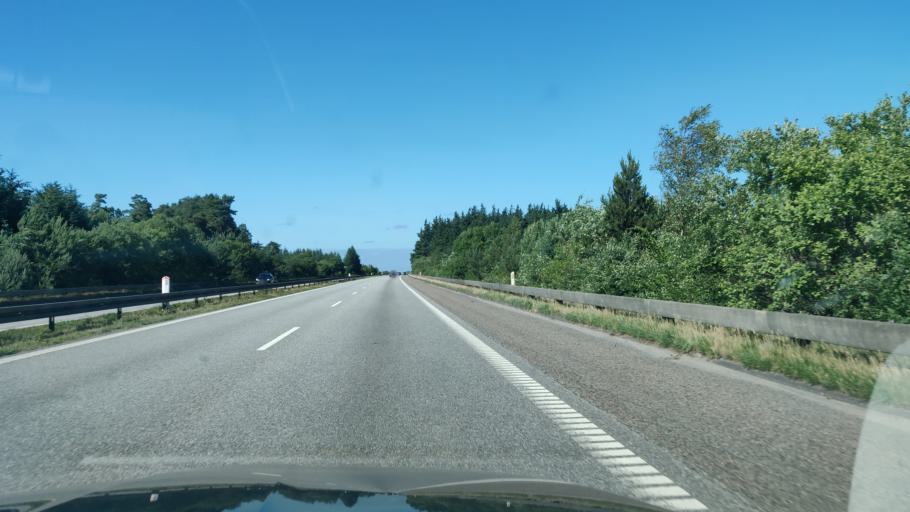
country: DK
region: North Denmark
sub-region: Alborg Kommune
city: Svenstrup
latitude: 56.9286
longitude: 9.8479
